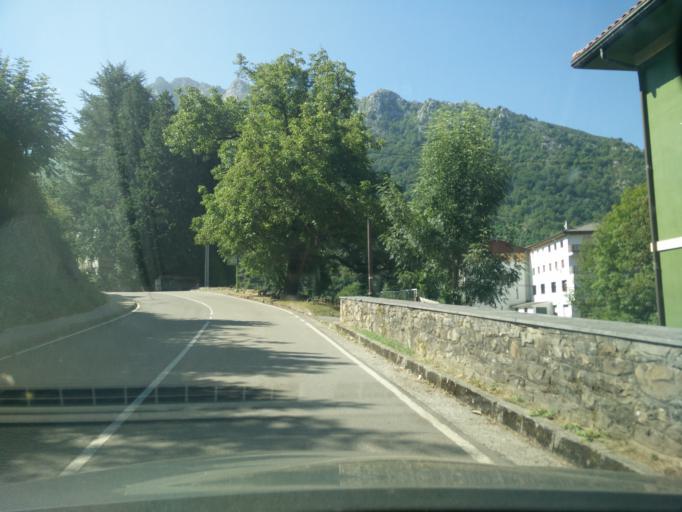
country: ES
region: Asturias
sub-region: Province of Asturias
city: Campo de Caso
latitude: 43.1822
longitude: -5.3441
